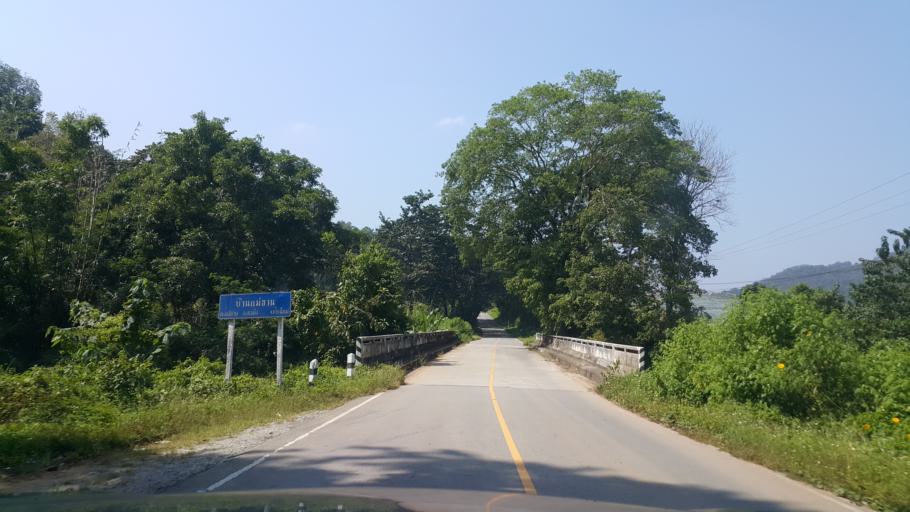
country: TH
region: Chiang Mai
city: Samoeng
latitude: 18.8606
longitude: 98.6472
